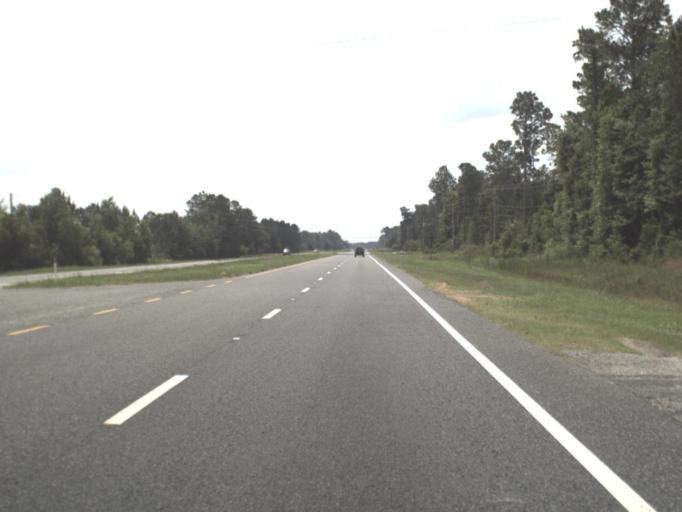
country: US
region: Florida
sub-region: Putnam County
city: East Palatka
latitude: 29.7920
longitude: -81.6496
